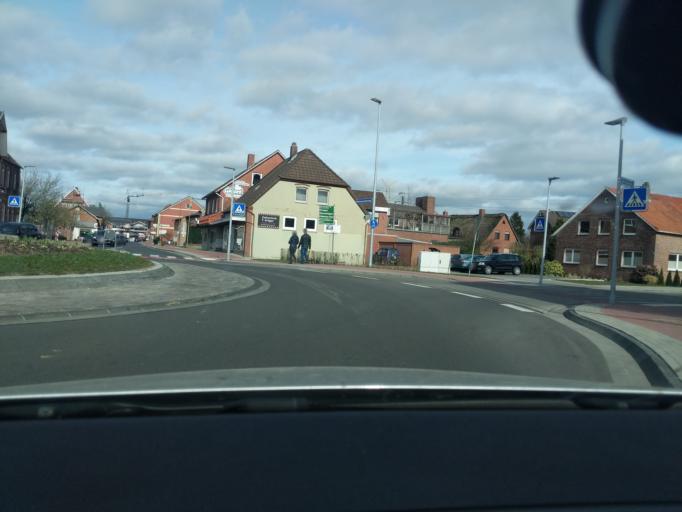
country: DE
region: Lower Saxony
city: Stade
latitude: 53.6514
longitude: 9.4823
